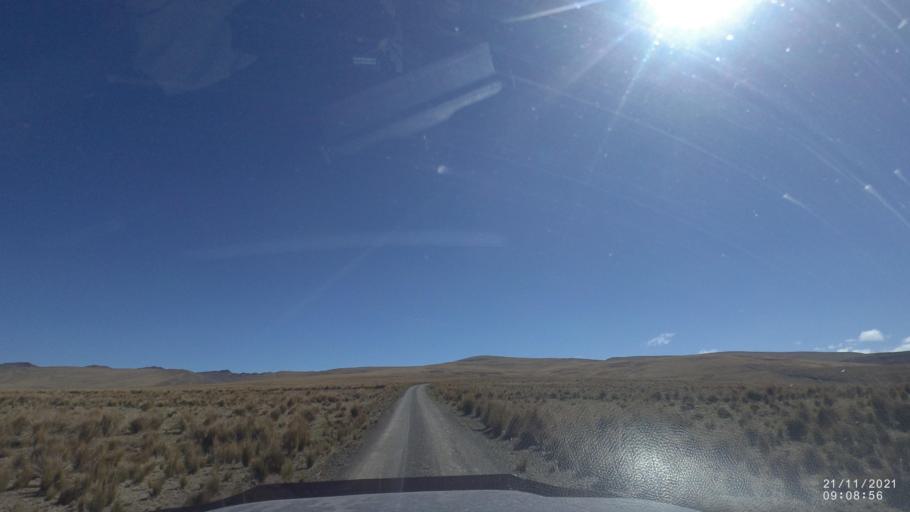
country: BO
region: Cochabamba
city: Cochabamba
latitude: -17.1603
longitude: -66.2648
